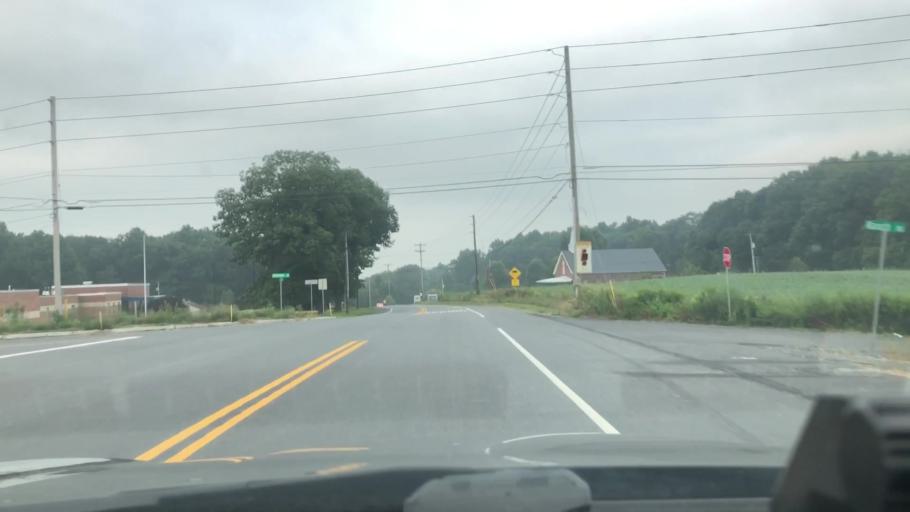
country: US
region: Pennsylvania
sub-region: Berks County
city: Kutztown
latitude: 40.5760
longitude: -75.8014
